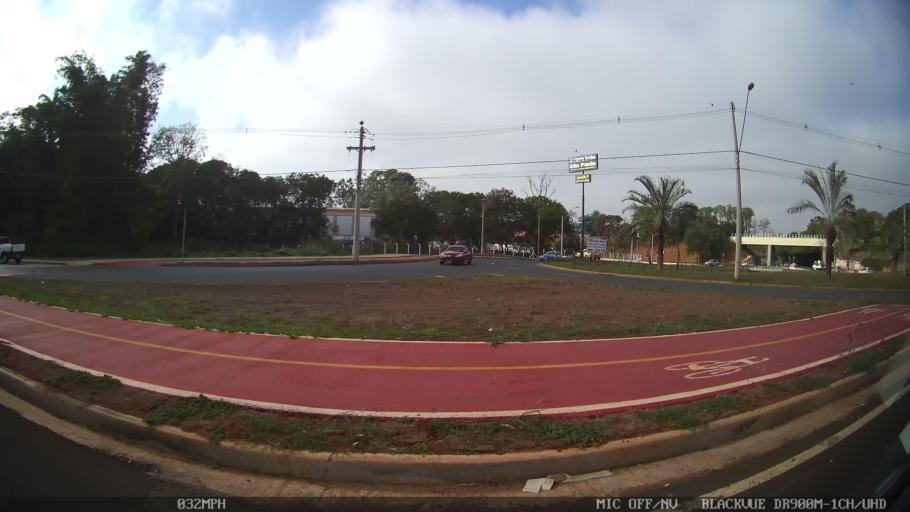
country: BR
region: Sao Paulo
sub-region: Sao Jose Do Rio Preto
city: Sao Jose do Rio Preto
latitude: -20.8142
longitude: -49.4348
